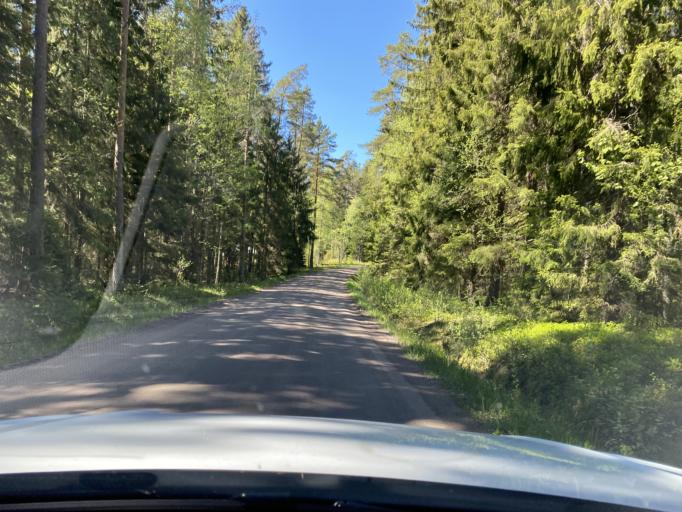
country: FI
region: Satakunta
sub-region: Rauma
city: Kiukainen
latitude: 61.1360
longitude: 21.9725
